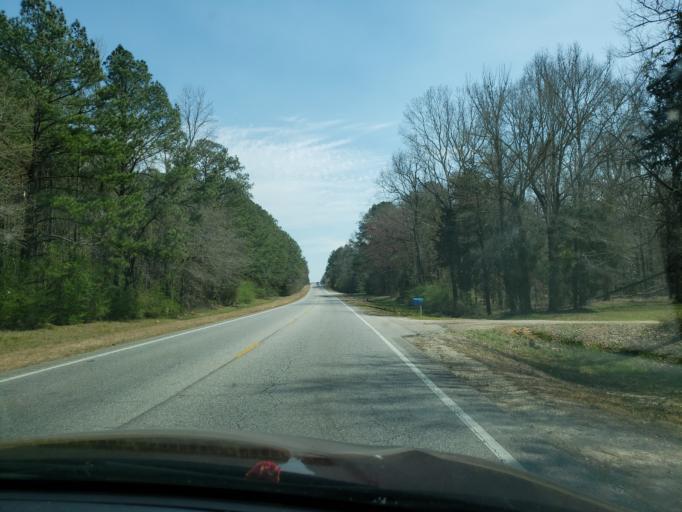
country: US
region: Alabama
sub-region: Elmore County
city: Elmore
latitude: 32.5436
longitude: -86.2740
